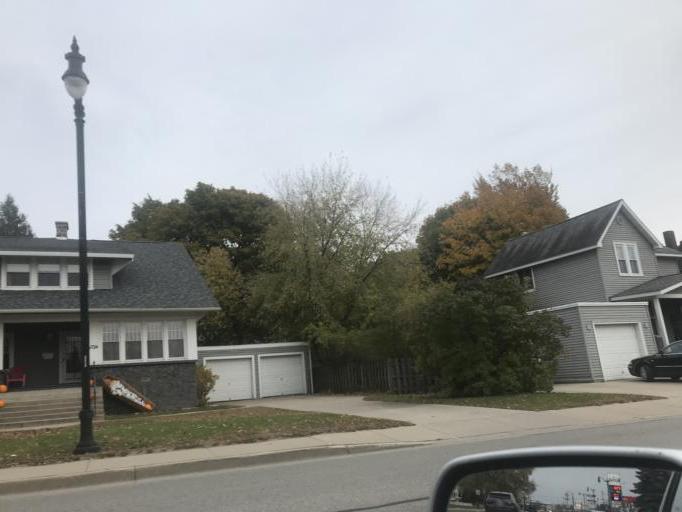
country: US
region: Michigan
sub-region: Menominee County
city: Menominee
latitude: 45.1153
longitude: -87.6143
